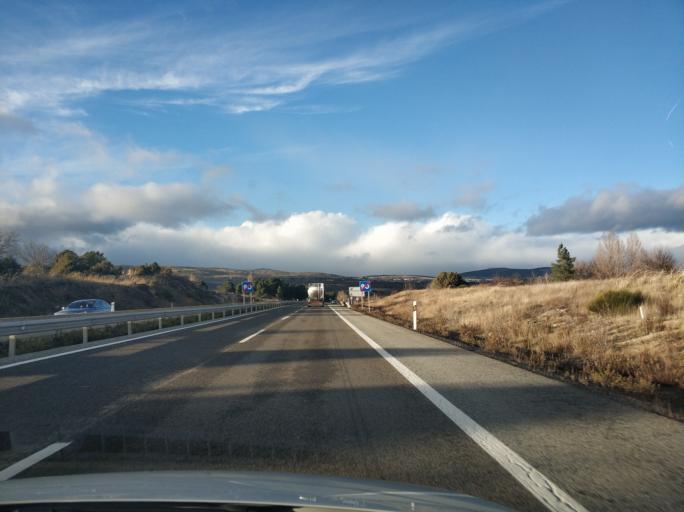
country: ES
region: Madrid
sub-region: Provincia de Madrid
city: La Cabrera
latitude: 40.8996
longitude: -3.6065
